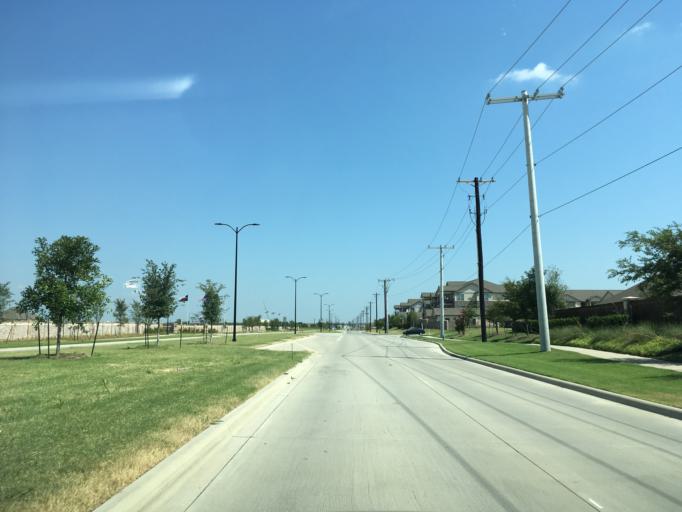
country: US
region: Texas
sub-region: Collin County
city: Prosper
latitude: 33.1969
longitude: -96.7677
